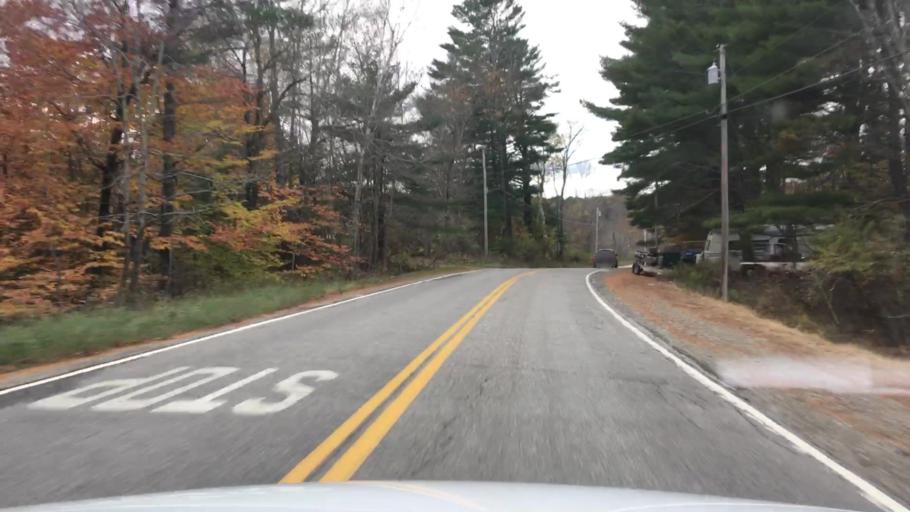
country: US
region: Maine
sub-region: Sagadahoc County
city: Richmond
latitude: 44.1050
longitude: -69.8951
